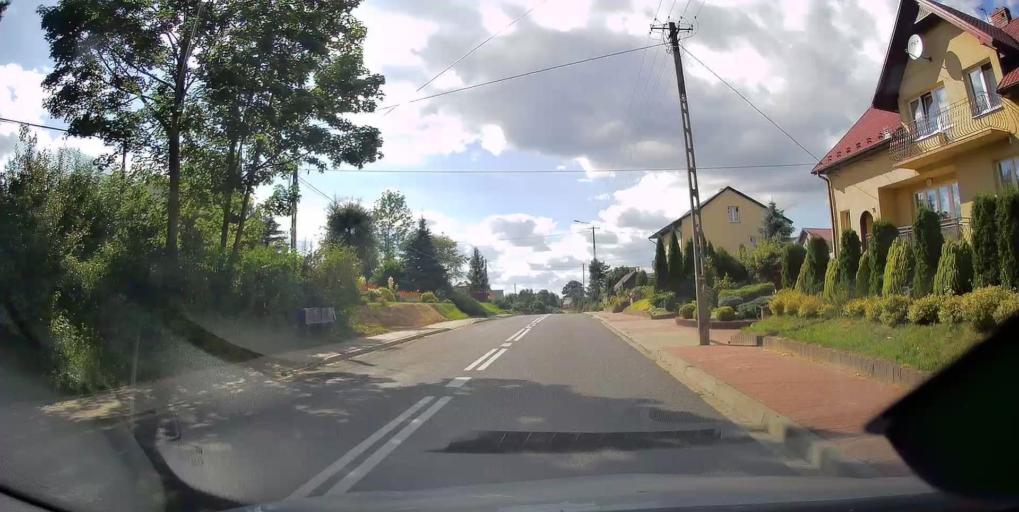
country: PL
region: Swietokrzyskie
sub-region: Powiat kielecki
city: Nowa Slupia
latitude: 50.8833
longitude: 21.0503
